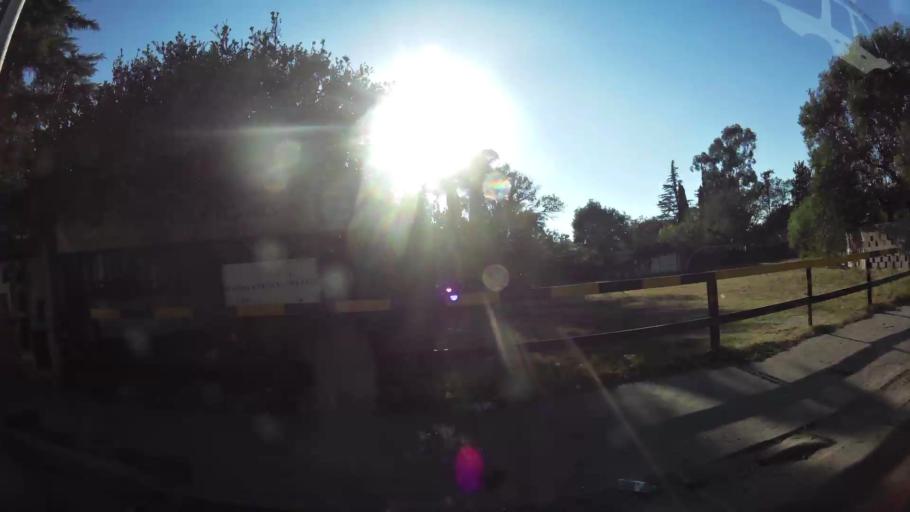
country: AR
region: Cordoba
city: Villa Allende
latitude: -31.3407
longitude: -64.2548
